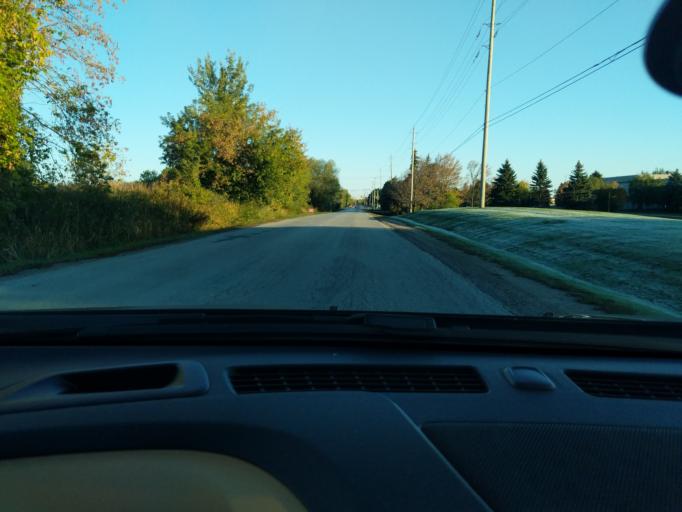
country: CA
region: Ontario
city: Collingwood
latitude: 44.4971
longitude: -80.2501
